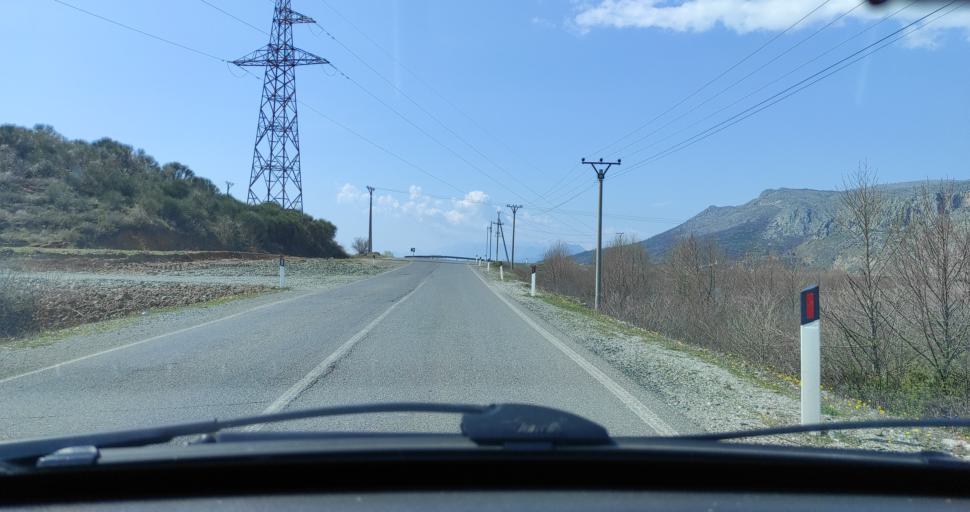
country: AL
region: Shkoder
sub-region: Rrethi i Shkodres
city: Vau i Dejes
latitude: 42.0022
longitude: 19.6286
